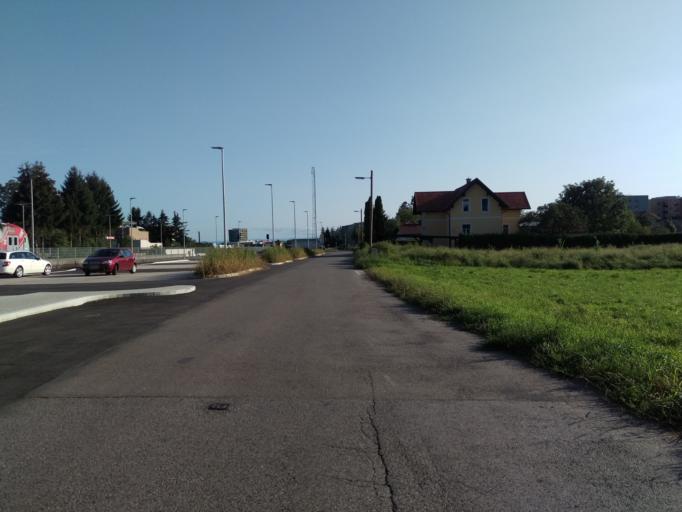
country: AT
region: Styria
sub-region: Politischer Bezirk Graz-Umgebung
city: Seiersberg
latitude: 47.0199
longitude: 15.4049
